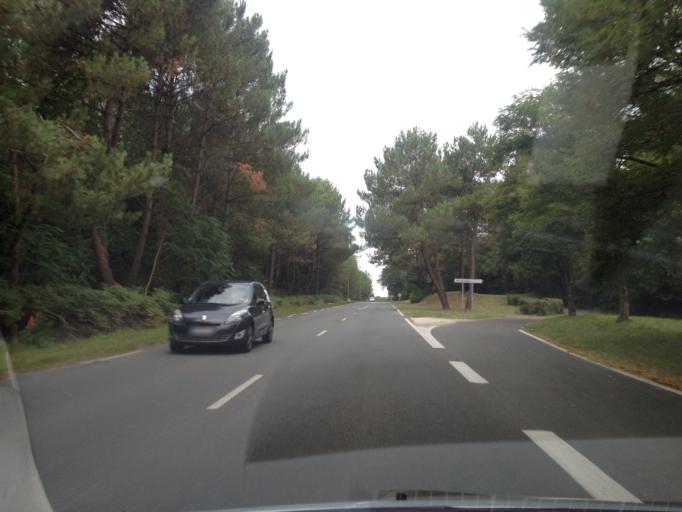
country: FR
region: Poitou-Charentes
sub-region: Departement de la Charente-Maritime
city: Saint-Palais-sur-Mer
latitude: 45.6551
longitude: -1.0976
